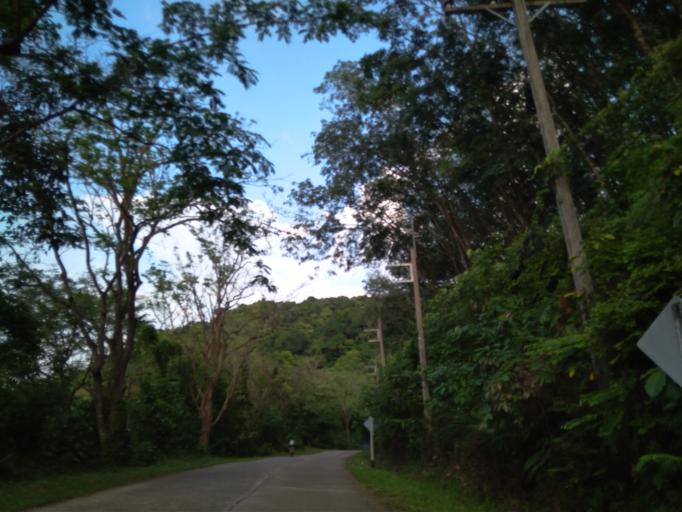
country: TH
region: Phangnga
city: Ko Yao
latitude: 8.1379
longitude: 98.6159
